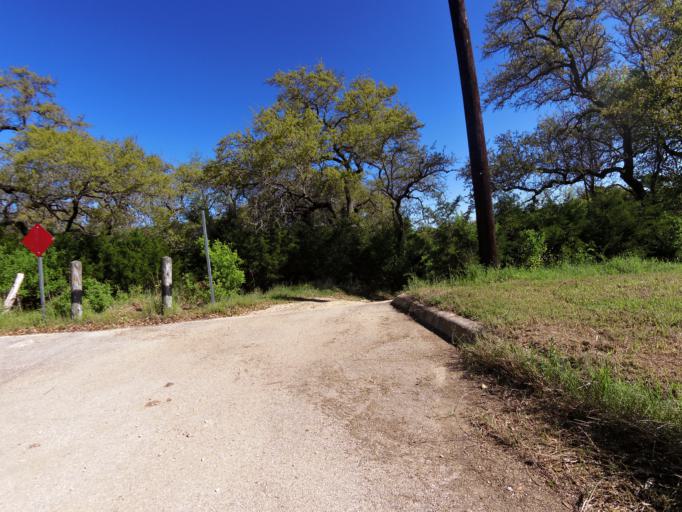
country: US
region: Texas
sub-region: Bexar County
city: Cross Mountain
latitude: 29.6766
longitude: -98.6427
